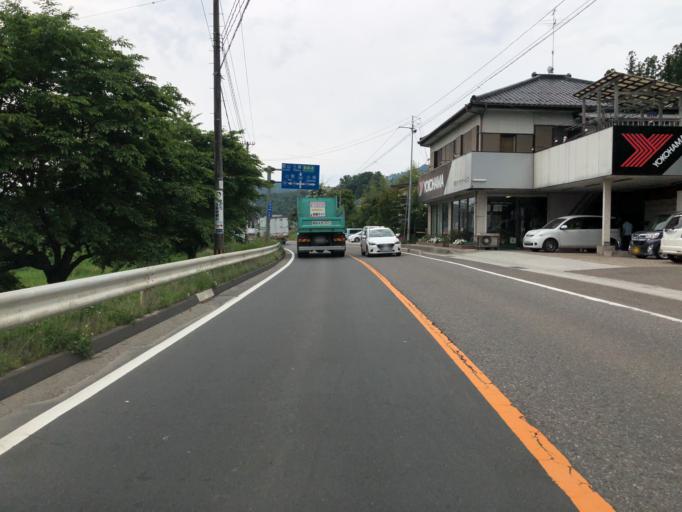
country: JP
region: Fukushima
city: Funehikimachi-funehiki
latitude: 37.4377
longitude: 140.5926
